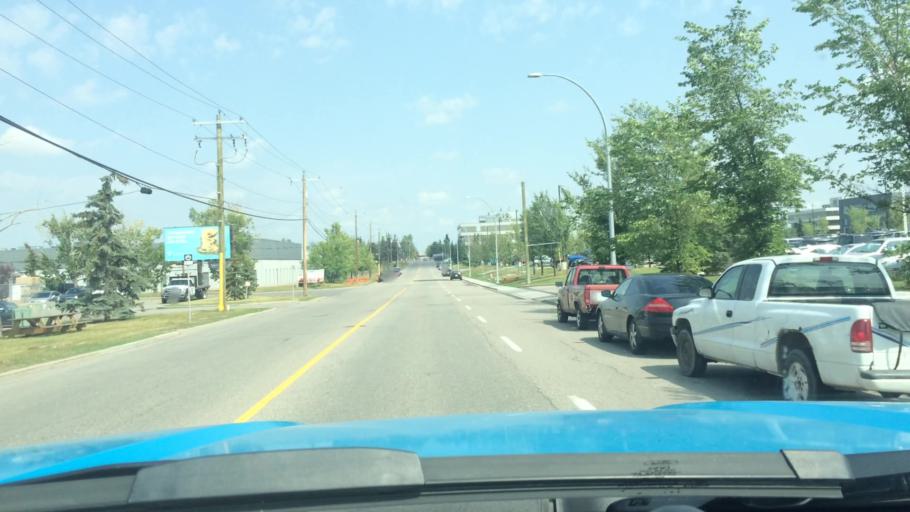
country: CA
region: Alberta
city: Calgary
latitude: 51.0831
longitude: -114.0051
